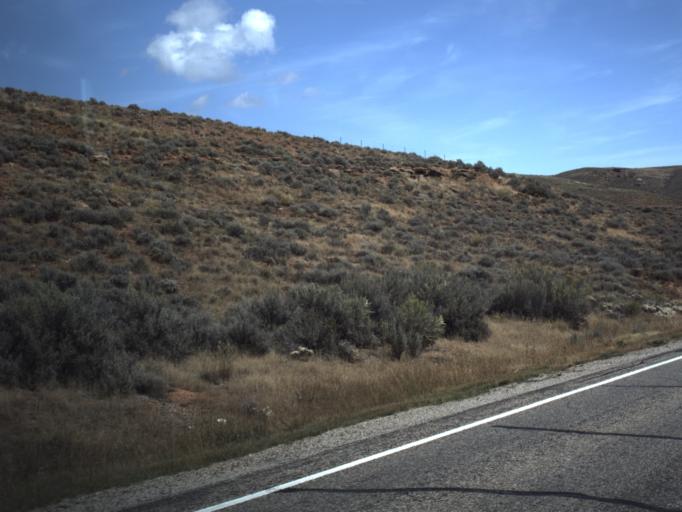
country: US
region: Utah
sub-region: Rich County
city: Randolph
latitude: 41.7764
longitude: -111.1854
